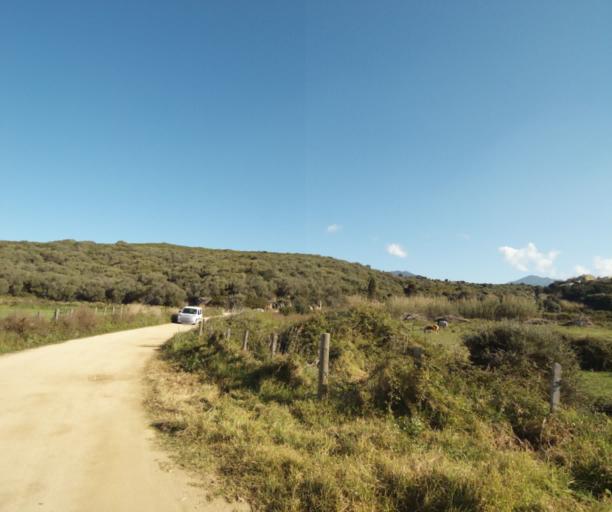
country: FR
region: Corsica
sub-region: Departement de la Corse-du-Sud
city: Propriano
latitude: 41.6641
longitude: 8.8929
